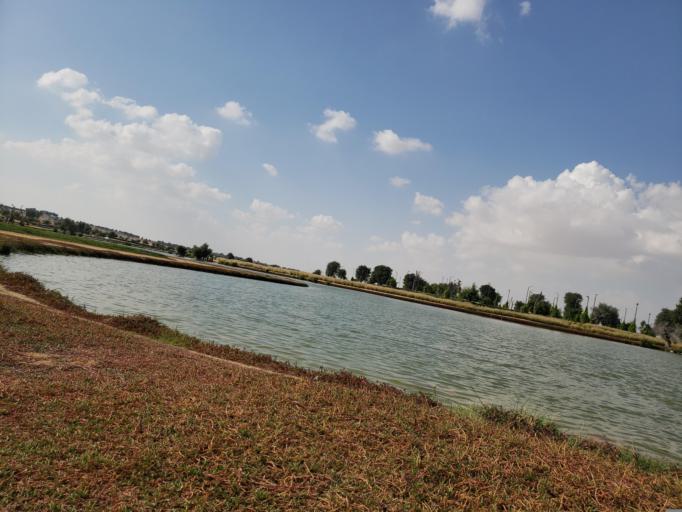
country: AE
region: Dubai
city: Dubai
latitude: 24.8550
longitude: 55.2504
